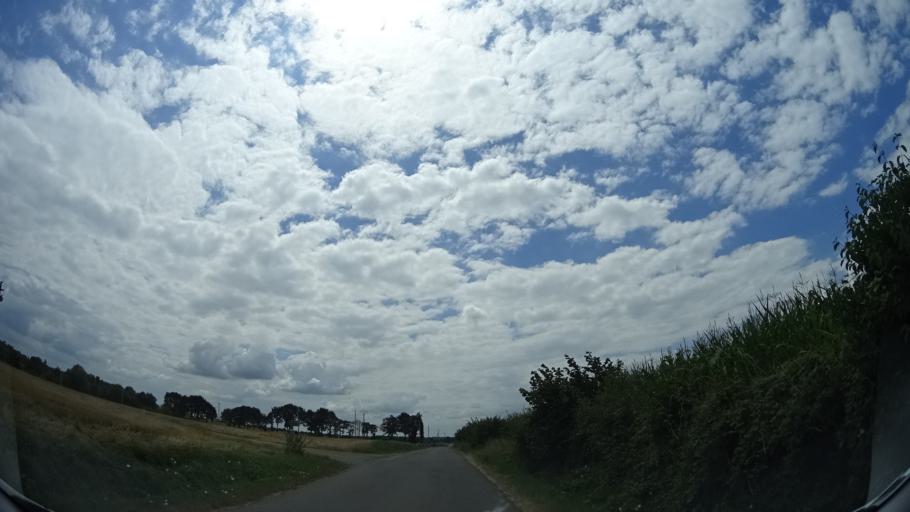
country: FR
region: Brittany
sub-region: Departement d'Ille-et-Vilaine
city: La Meziere
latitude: 48.1882
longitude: -1.7669
